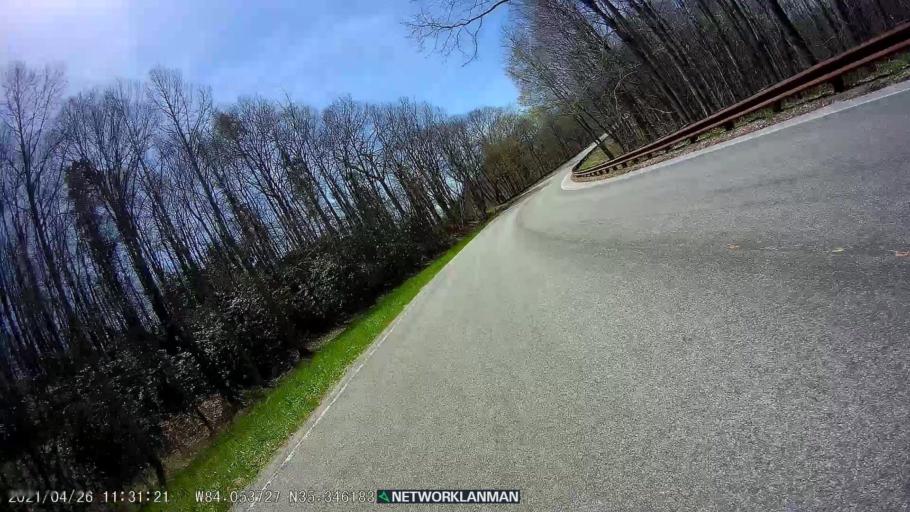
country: US
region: North Carolina
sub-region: Graham County
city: Robbinsville
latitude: 35.3462
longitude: -84.0537
